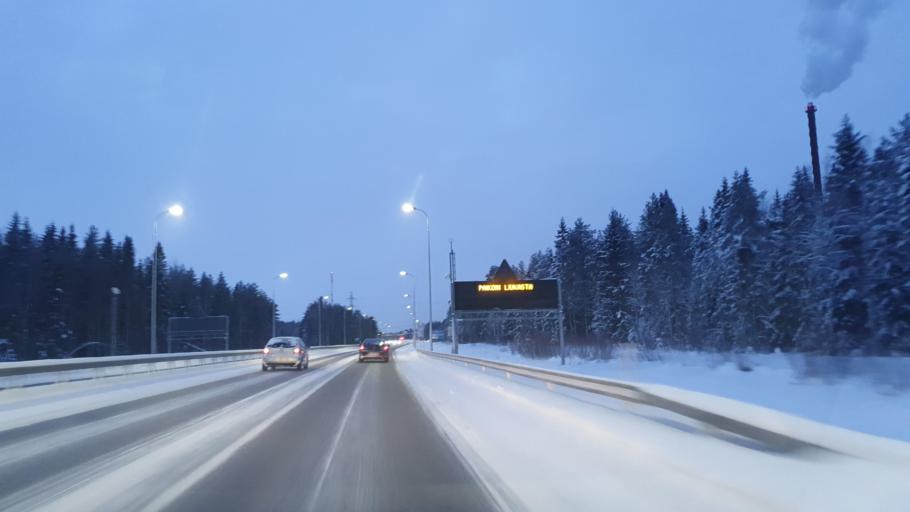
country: FI
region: Northern Ostrobothnia
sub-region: Oulu
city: Oulu
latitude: 64.9859
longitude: 25.5467
